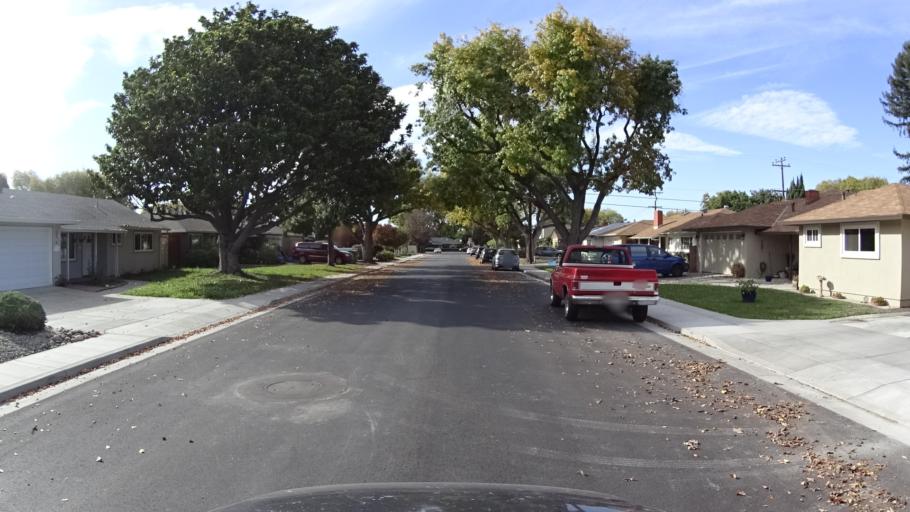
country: US
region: California
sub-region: Santa Clara County
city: Santa Clara
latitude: 37.3551
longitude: -121.9660
